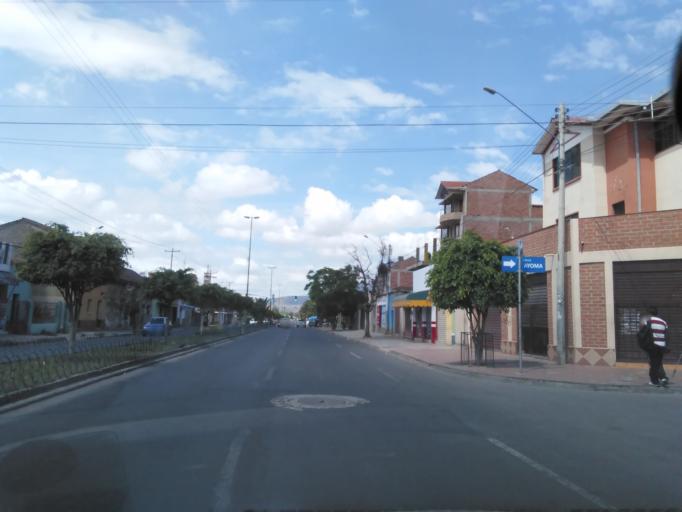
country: BO
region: Cochabamba
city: Cochabamba
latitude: -17.4129
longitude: -66.1651
